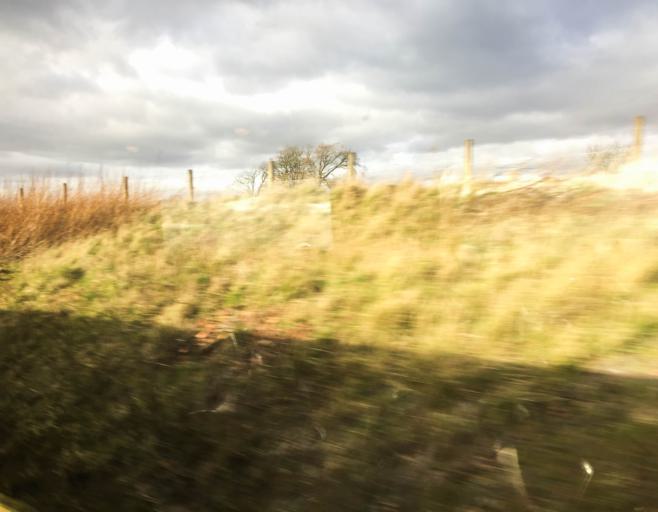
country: GB
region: Scotland
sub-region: South Lanarkshire
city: Carluke
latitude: 55.7033
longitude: -3.8140
